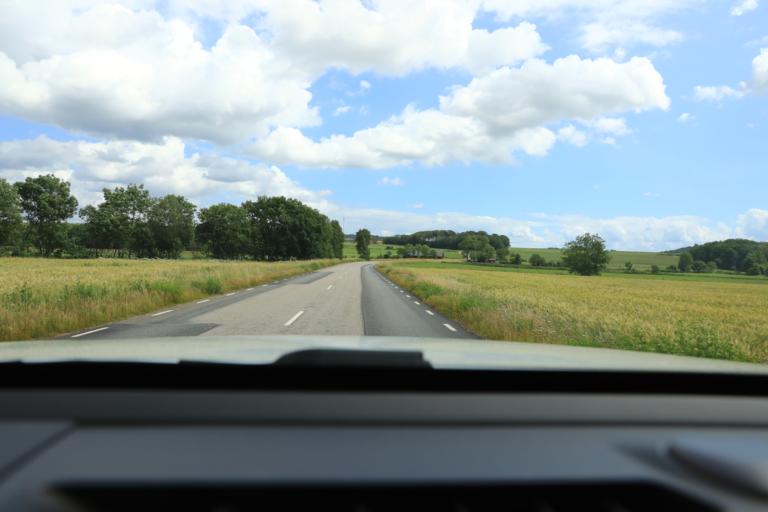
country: SE
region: Halland
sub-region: Varbergs Kommun
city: Tvaaker
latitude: 57.0321
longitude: 12.4503
